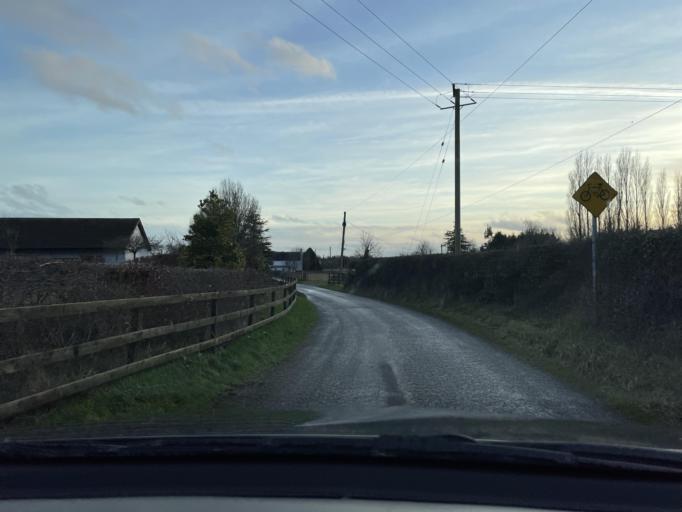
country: IE
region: Leinster
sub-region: Kilkenny
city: Thomastown
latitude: 52.6474
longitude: -7.1137
